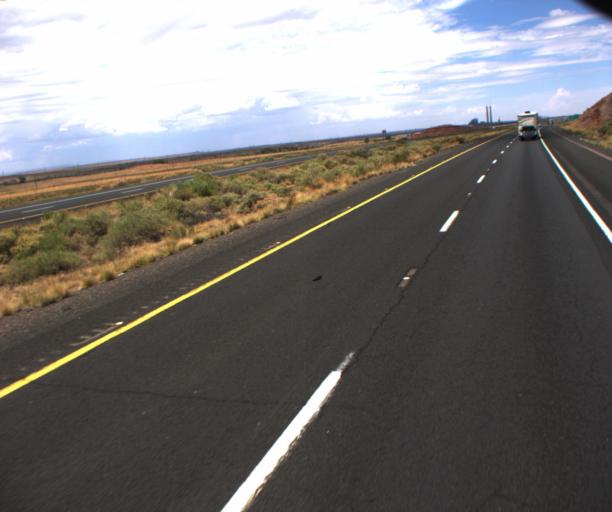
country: US
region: Arizona
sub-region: Navajo County
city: Holbrook
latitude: 34.9155
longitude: -110.2491
